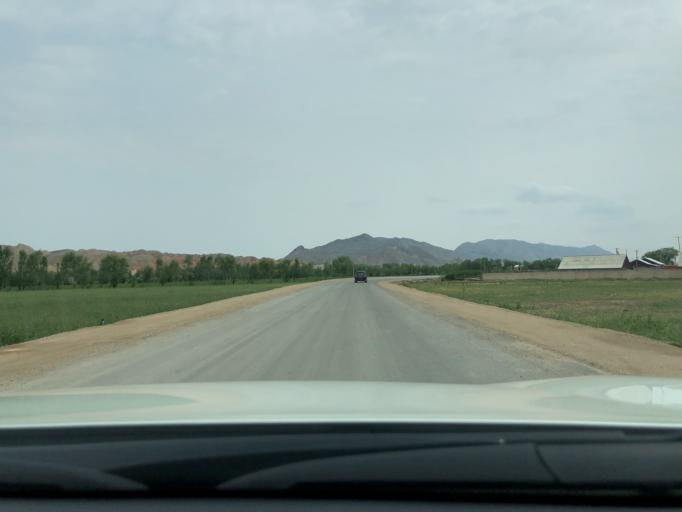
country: TJ
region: Viloyati Sughd
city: Isfara
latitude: 40.1511
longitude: 70.6183
